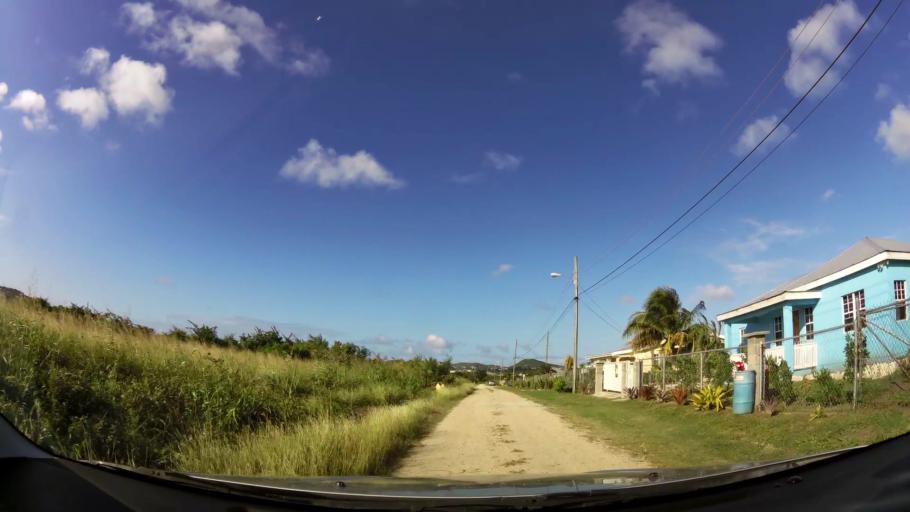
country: AG
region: Saint George
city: Piggotts
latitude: 17.1002
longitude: -61.8050
